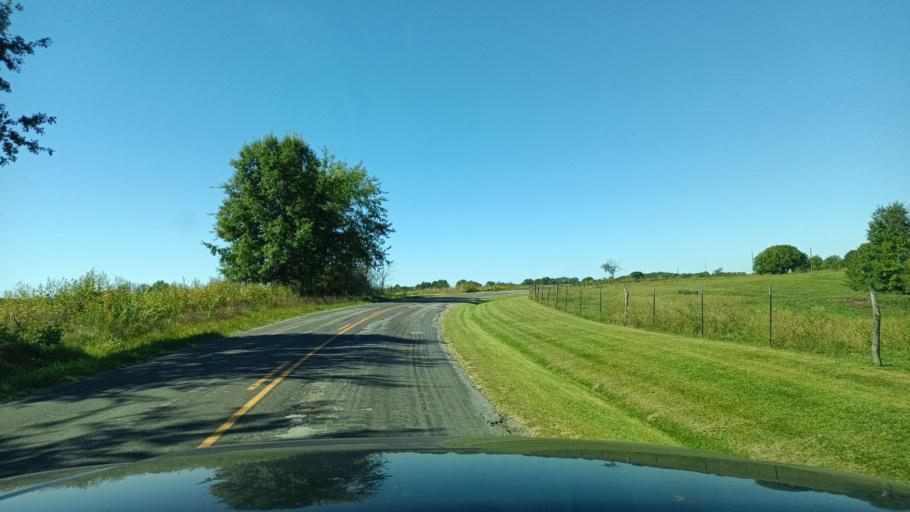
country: US
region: Missouri
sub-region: Scotland County
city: Memphis
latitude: 40.3536
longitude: -92.2666
